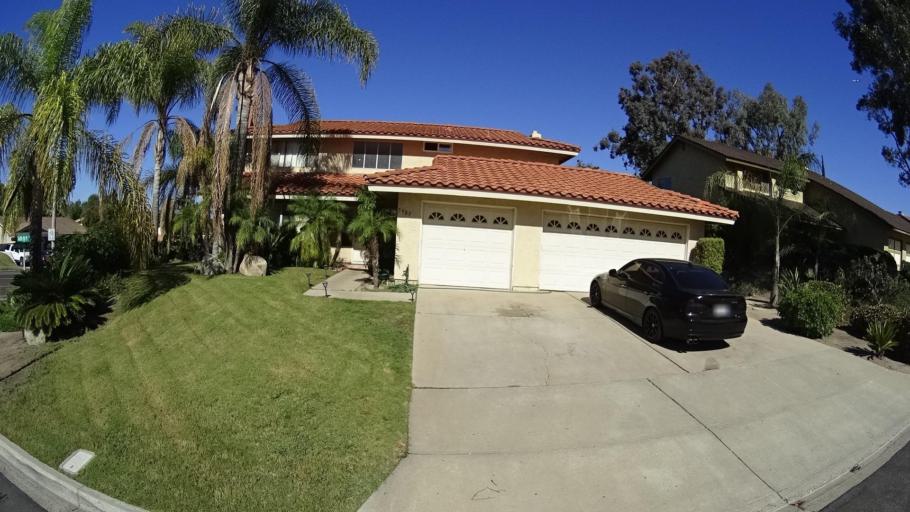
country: US
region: California
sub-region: San Diego County
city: Bonita
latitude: 32.6654
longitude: -117.0018
